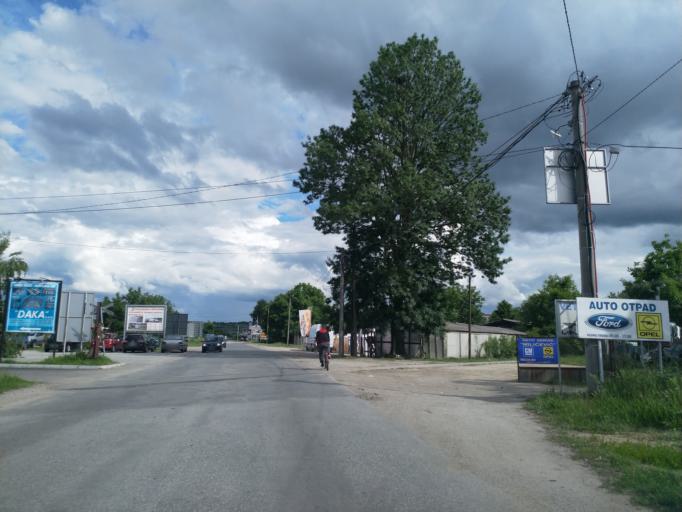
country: RS
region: Central Serbia
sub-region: Pomoravski Okrug
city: Jagodina
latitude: 43.9627
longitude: 21.2801
